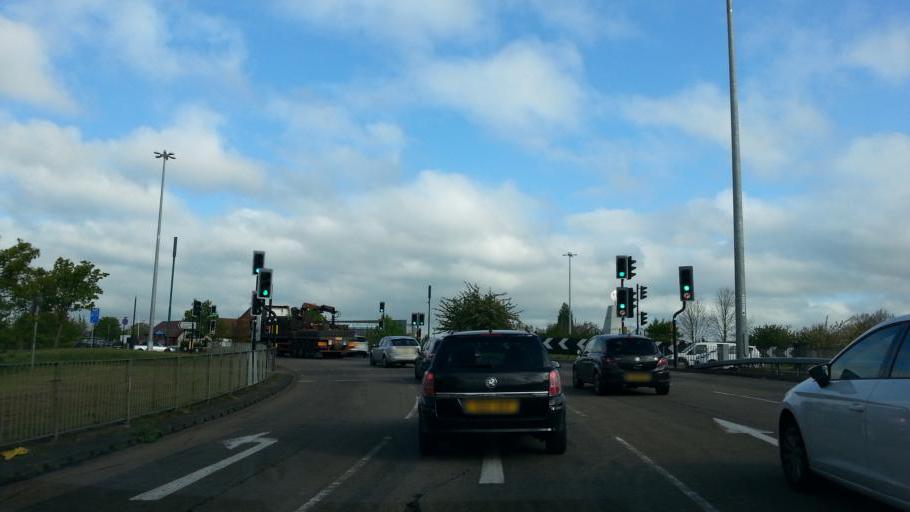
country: GB
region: England
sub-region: Coventry
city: Coventry
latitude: 52.4294
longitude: -1.4855
